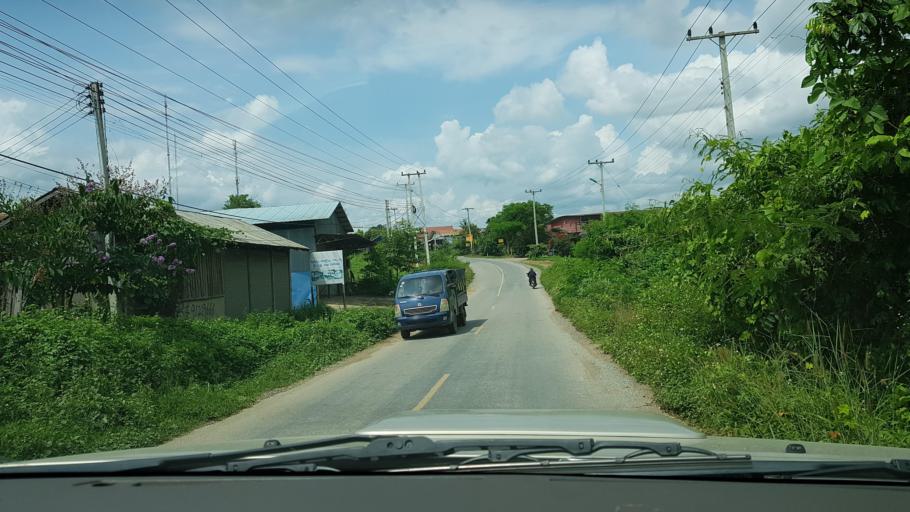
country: LA
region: Loungnamtha
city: Muang Nale
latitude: 20.1389
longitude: 101.4531
